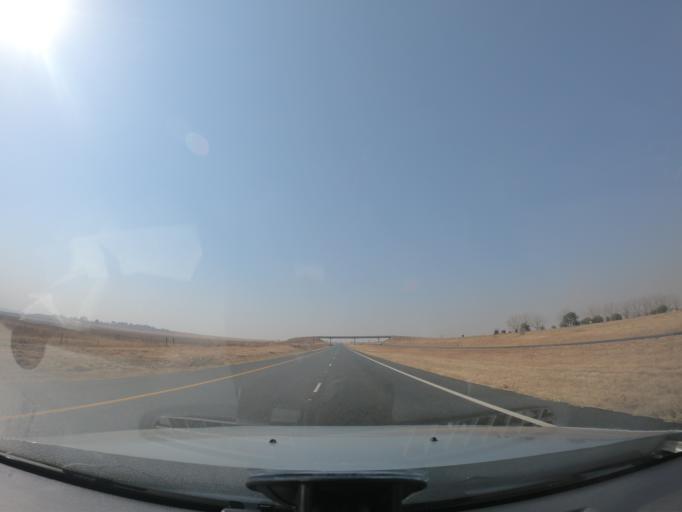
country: ZA
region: Gauteng
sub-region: City of Tshwane Metropolitan Municipality
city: Bronkhorstspruit
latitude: -25.8289
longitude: 28.7831
